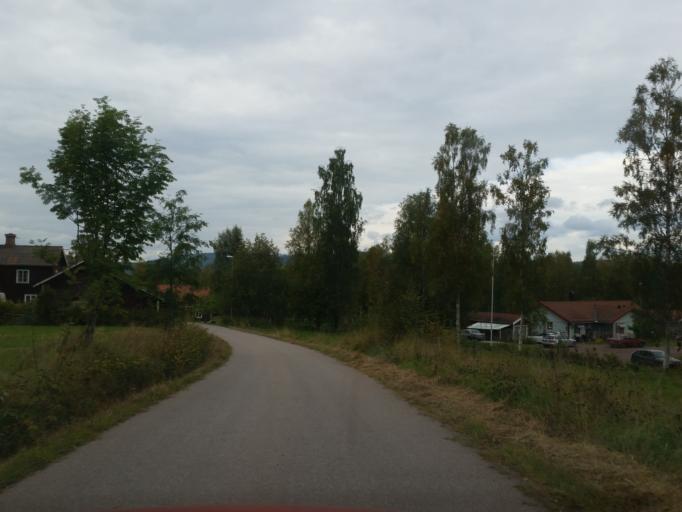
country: SE
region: Dalarna
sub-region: Leksand Municipality
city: Smedby
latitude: 60.6729
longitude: 15.1257
